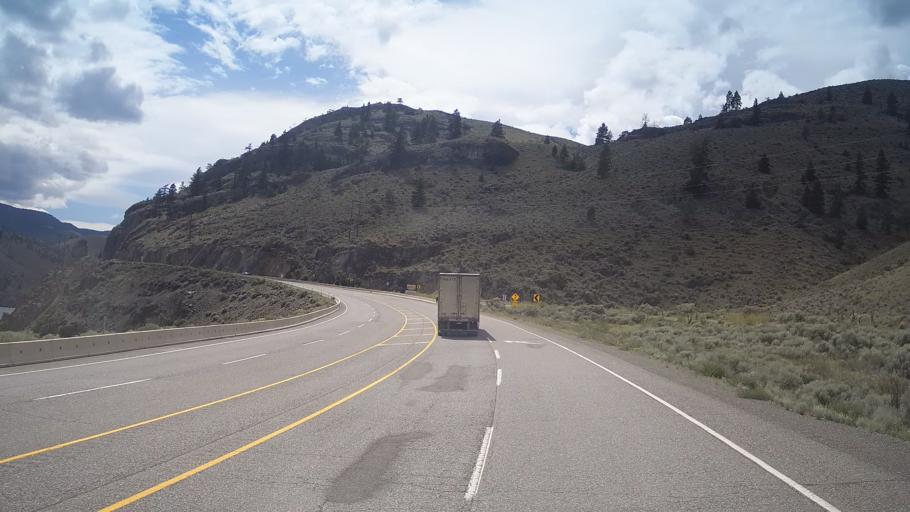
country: CA
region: British Columbia
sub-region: Thompson-Nicola Regional District
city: Ashcroft
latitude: 50.5085
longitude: -121.2858
